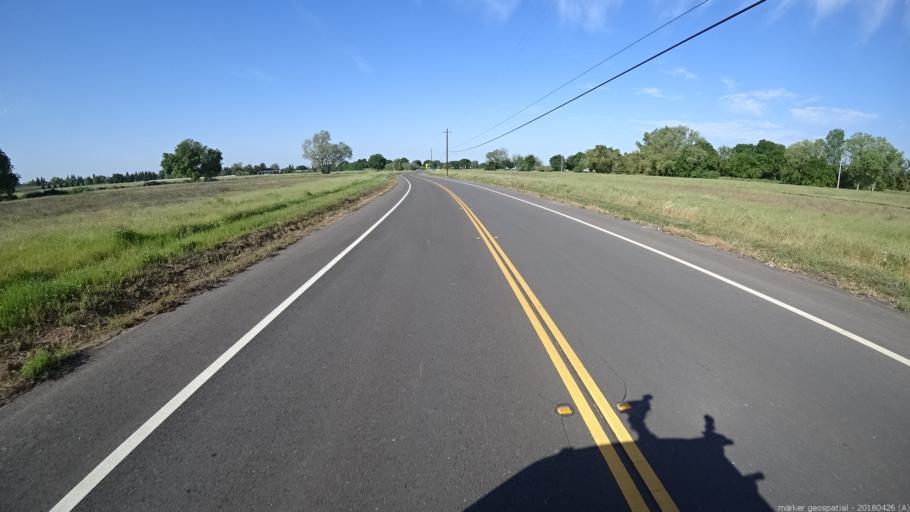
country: US
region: California
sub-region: Yolo County
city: West Sacramento
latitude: 38.5236
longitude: -121.5465
